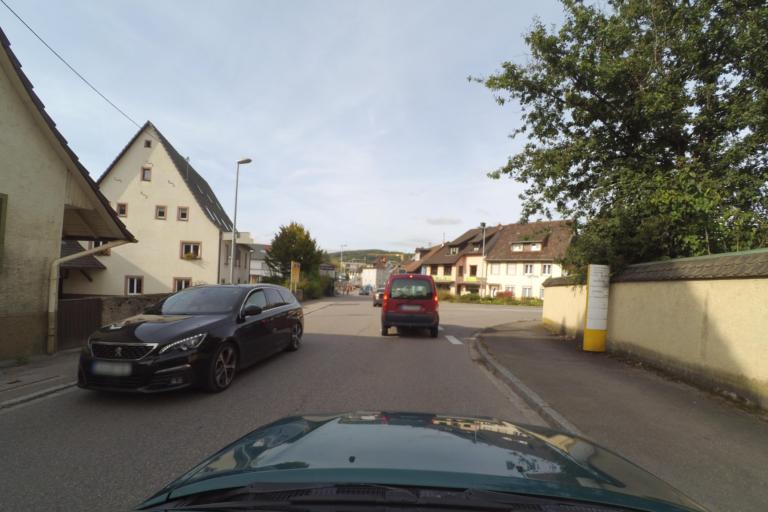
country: DE
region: Baden-Wuerttemberg
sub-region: Freiburg Region
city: Kandern
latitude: 47.7114
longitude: 7.6595
